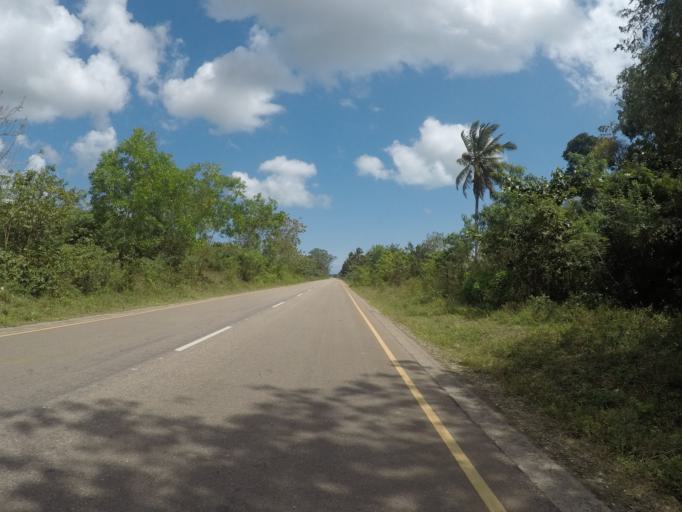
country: TZ
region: Zanzibar Central/South
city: Koani
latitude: -6.2377
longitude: 39.3586
